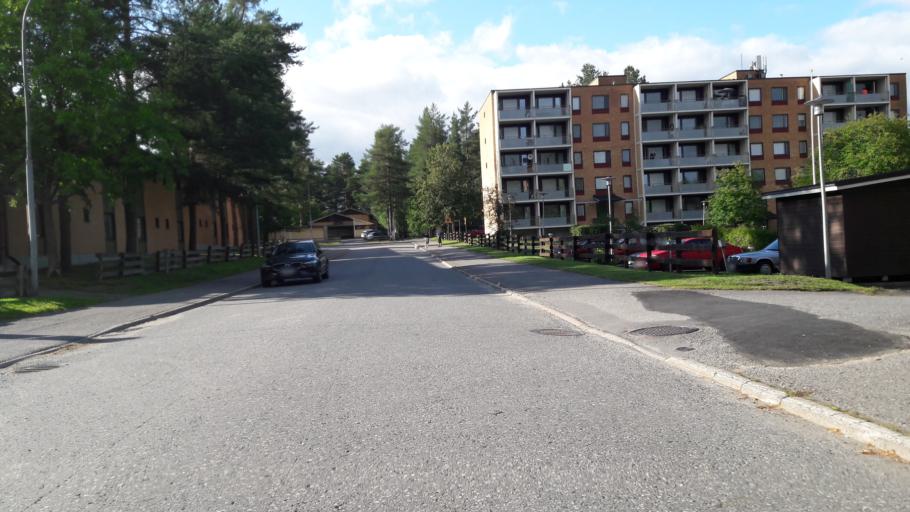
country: FI
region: North Karelia
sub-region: Joensuu
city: Joensuu
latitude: 62.6049
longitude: 29.7991
